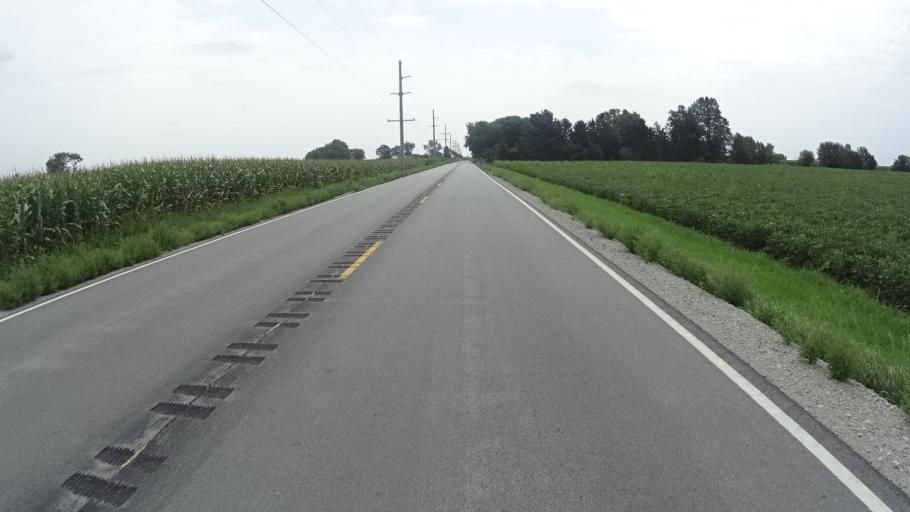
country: US
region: Indiana
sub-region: Madison County
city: Ingalls
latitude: 40.0144
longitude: -85.8166
